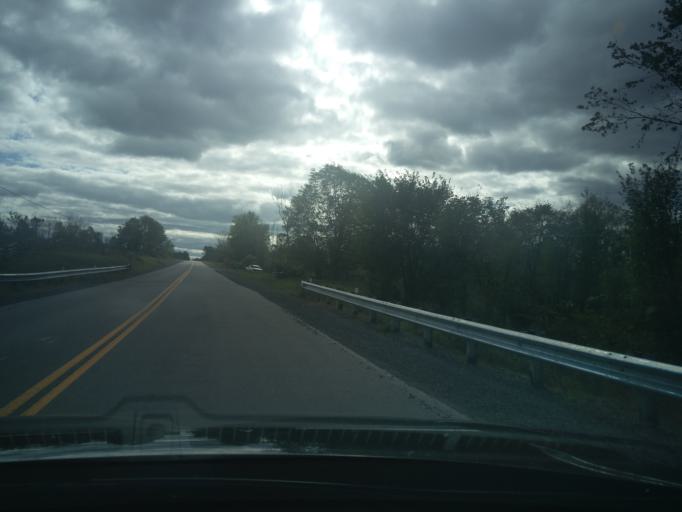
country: CA
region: Ontario
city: Perth
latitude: 44.7314
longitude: -76.3970
